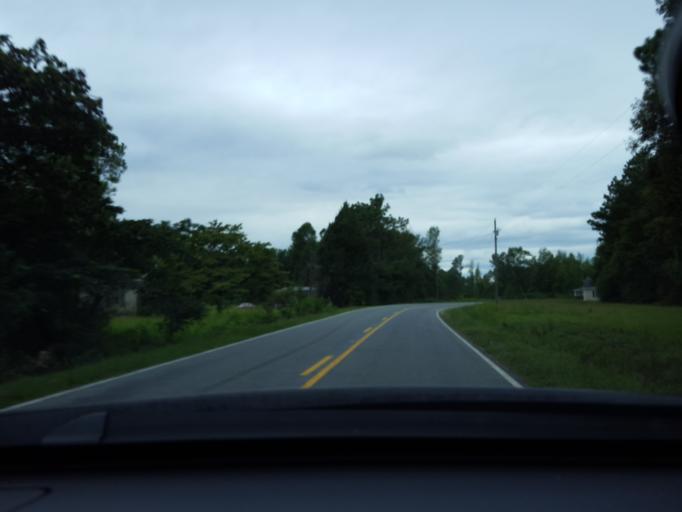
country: US
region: North Carolina
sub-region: Sampson County
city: Clinton
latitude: 34.7775
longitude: -78.3525
